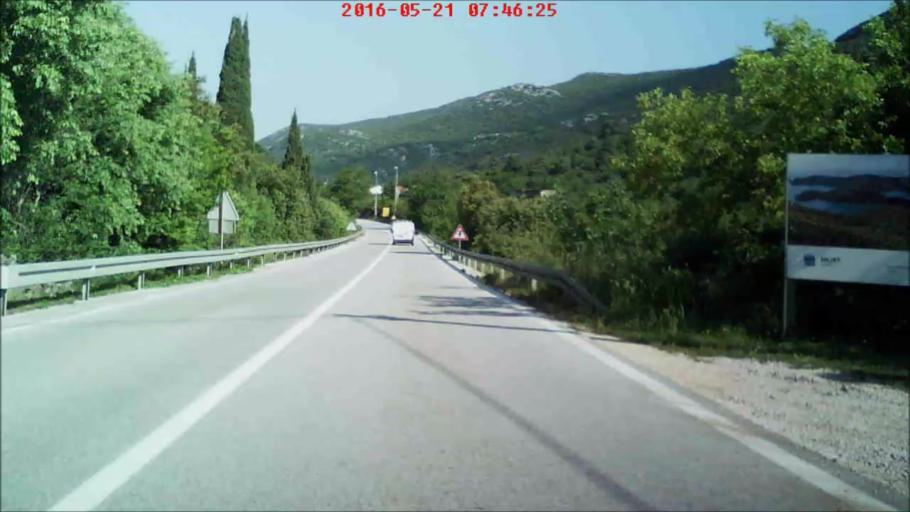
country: HR
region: Dubrovacko-Neretvanska
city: Ston
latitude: 42.8294
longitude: 17.7531
